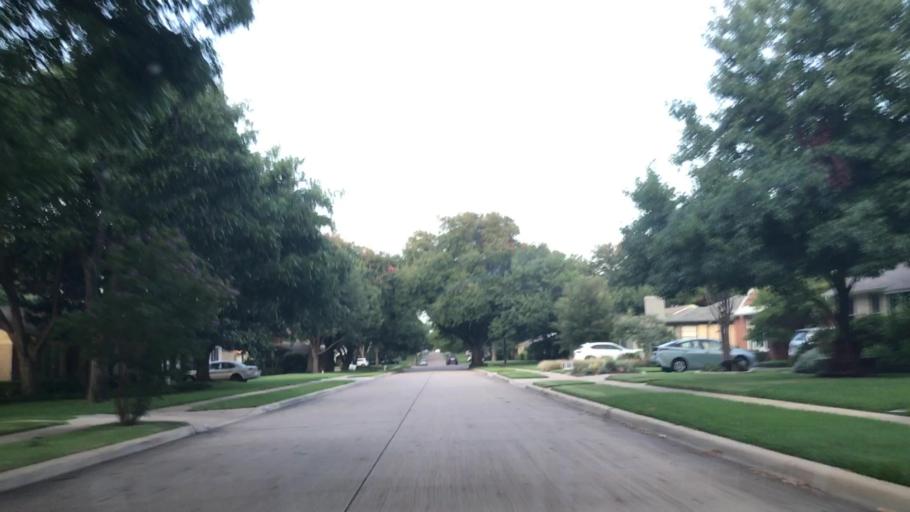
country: US
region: Texas
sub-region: Dallas County
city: Highland Park
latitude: 32.8392
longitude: -96.7595
